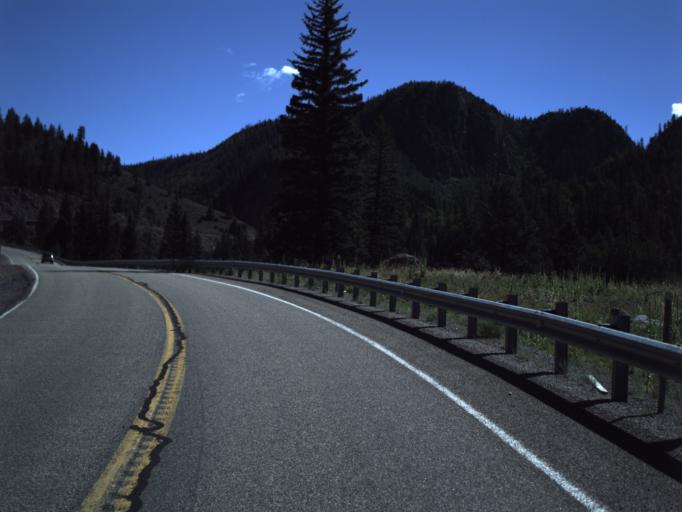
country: US
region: Utah
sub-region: Beaver County
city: Beaver
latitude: 38.2805
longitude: -112.4550
